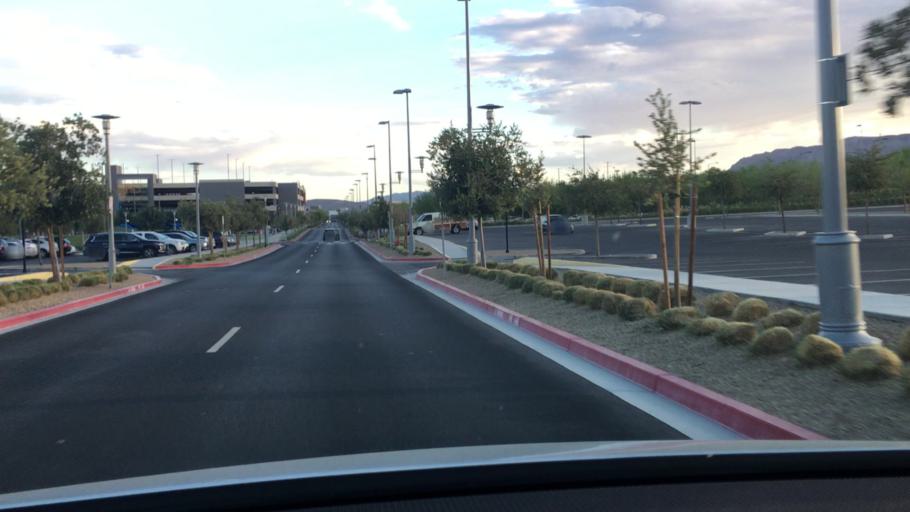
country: US
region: Nevada
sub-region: Clark County
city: Summerlin South
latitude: 36.1529
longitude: -115.3351
